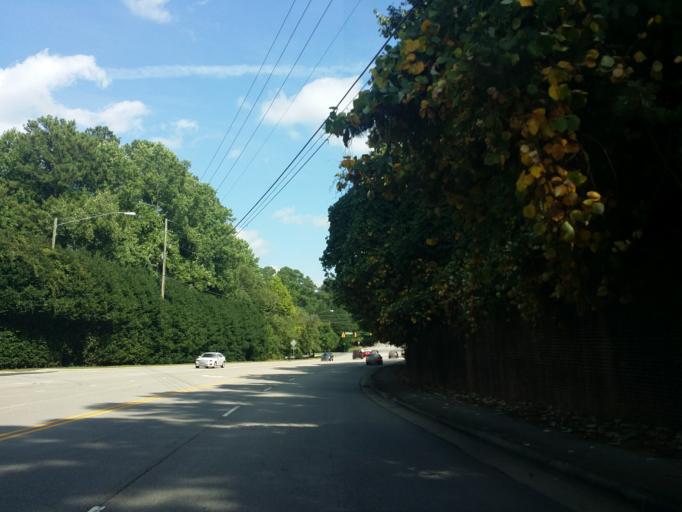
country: US
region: North Carolina
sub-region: Wake County
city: West Raleigh
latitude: 35.8626
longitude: -78.6972
